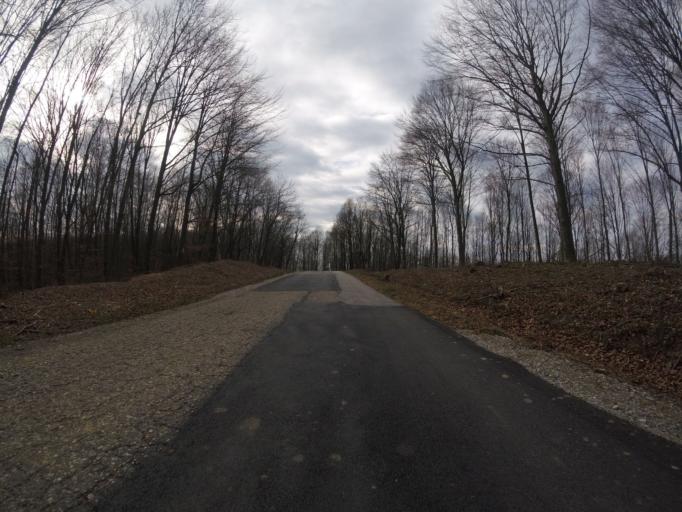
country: HR
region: Zagrebacka
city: Mraclin
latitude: 45.5234
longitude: 16.0483
